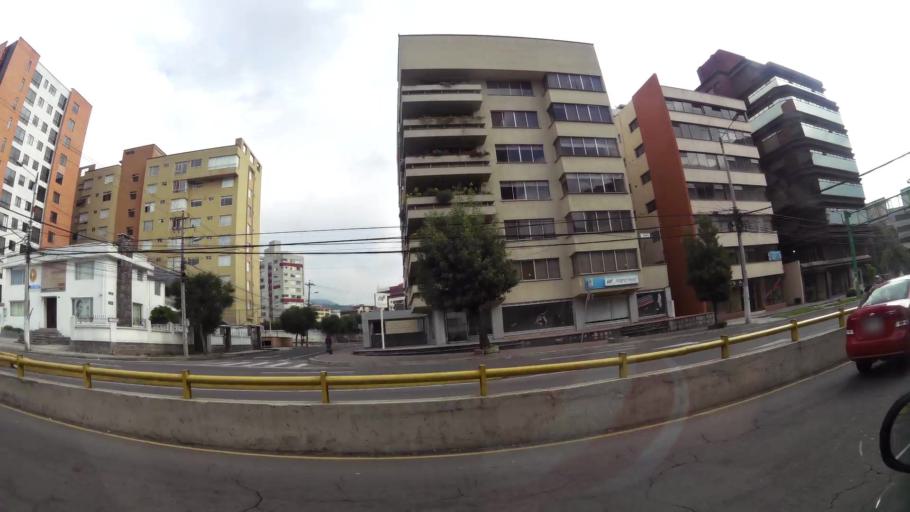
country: EC
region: Pichincha
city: Quito
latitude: -0.1821
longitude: -78.4877
